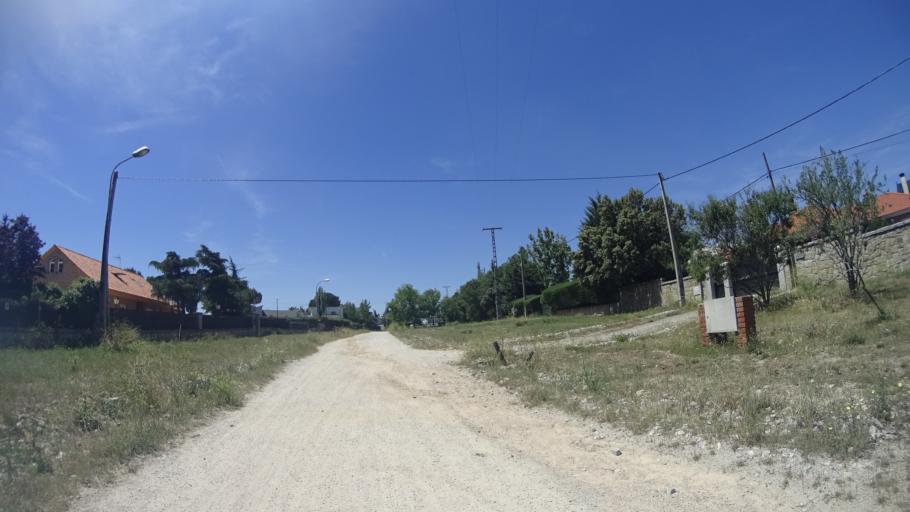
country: ES
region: Madrid
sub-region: Provincia de Madrid
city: Navalquejigo
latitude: 40.6219
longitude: -4.0313
